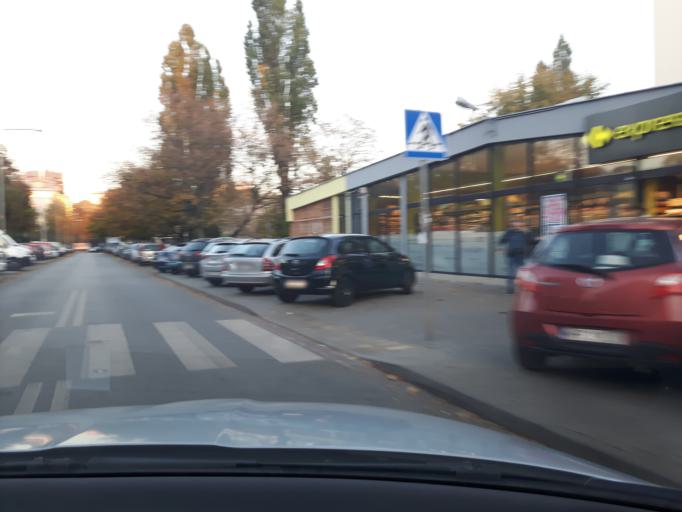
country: PL
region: Masovian Voivodeship
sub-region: Warszawa
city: Mokotow
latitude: 52.1932
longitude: 21.0077
